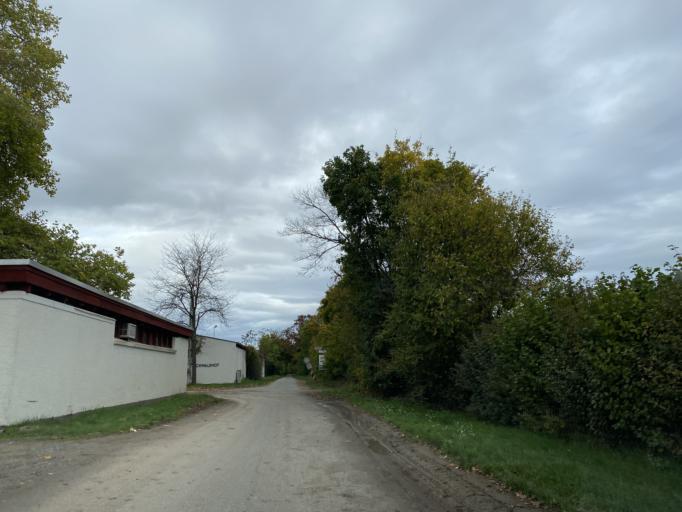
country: DE
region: Hesse
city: Griesheim
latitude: 49.8355
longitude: 8.5750
